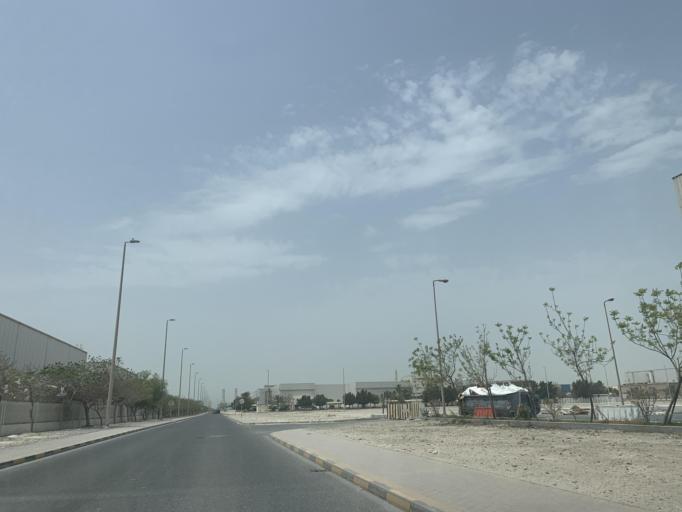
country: BH
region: Muharraq
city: Al Hadd
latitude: 26.2164
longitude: 50.6762
